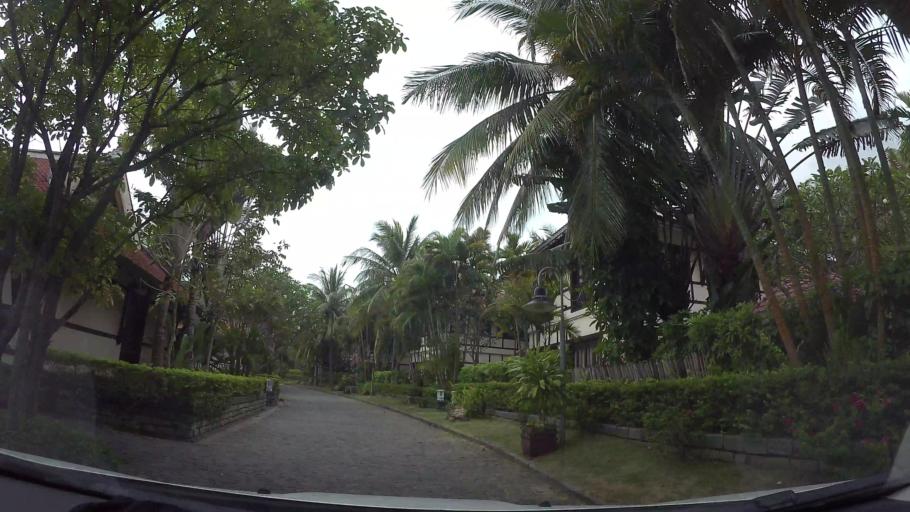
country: VN
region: Da Nang
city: Son Tra
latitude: 16.1061
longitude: 108.2948
